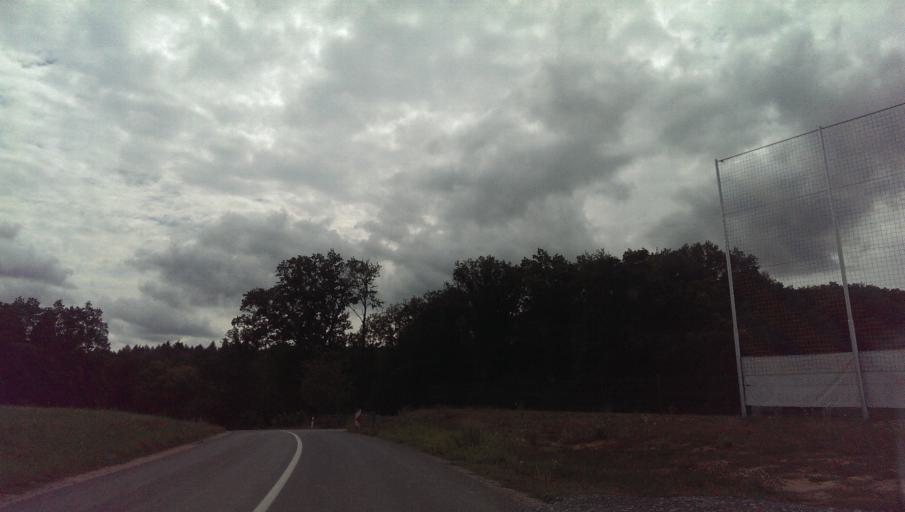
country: CZ
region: South Moravian
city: Velka nad Velickou
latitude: 48.8991
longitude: 17.5630
